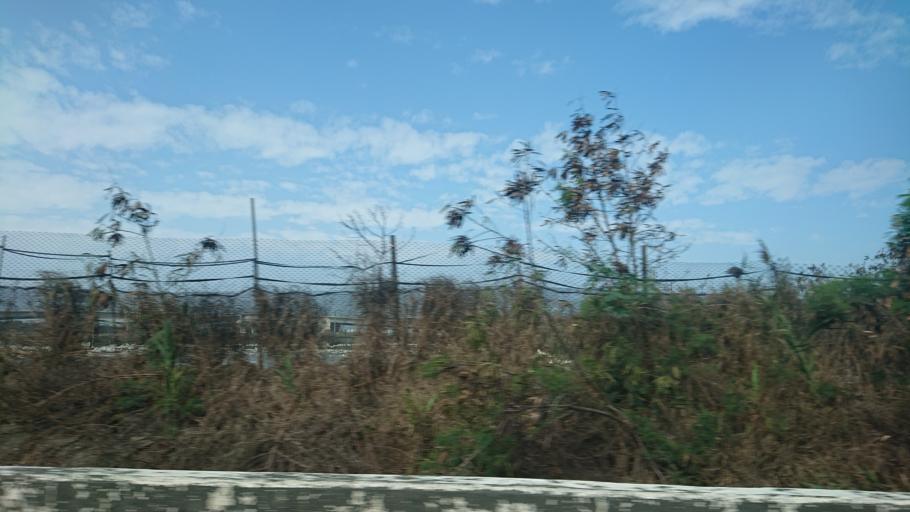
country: TW
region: Taiwan
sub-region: Changhua
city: Chang-hua
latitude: 23.9354
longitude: 120.3238
